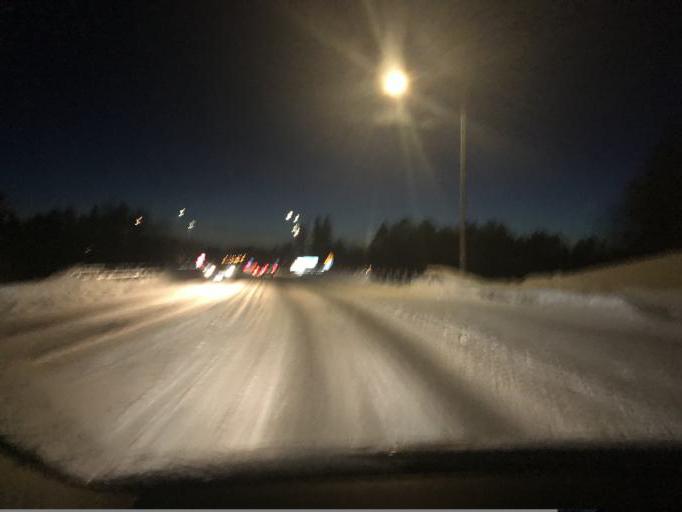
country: SE
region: Norrbotten
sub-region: Lulea Kommun
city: Gammelstad
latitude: 65.6343
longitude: 22.0373
